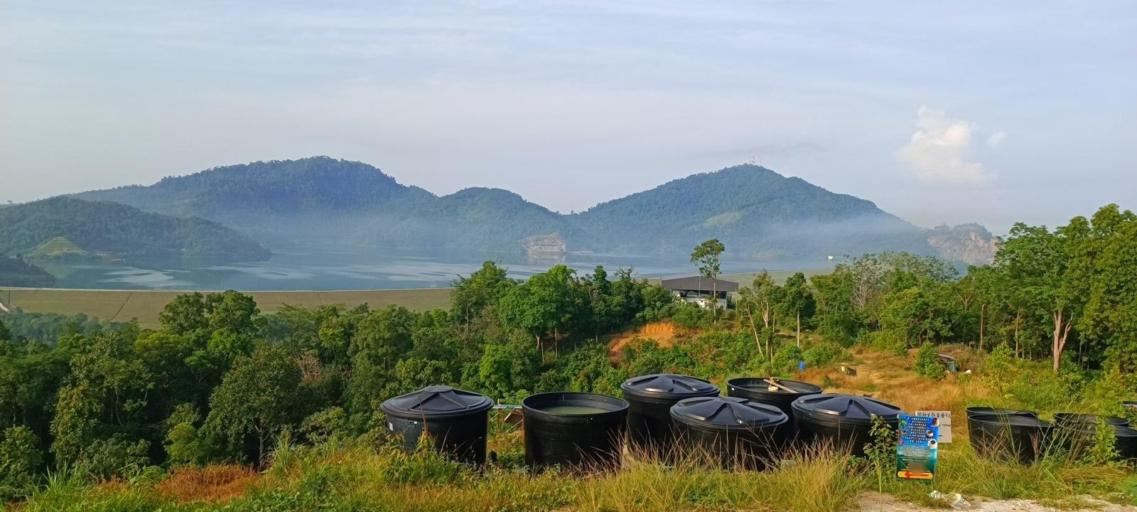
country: MY
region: Penang
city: Bukit Mertajam
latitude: 5.4047
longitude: 100.5096
